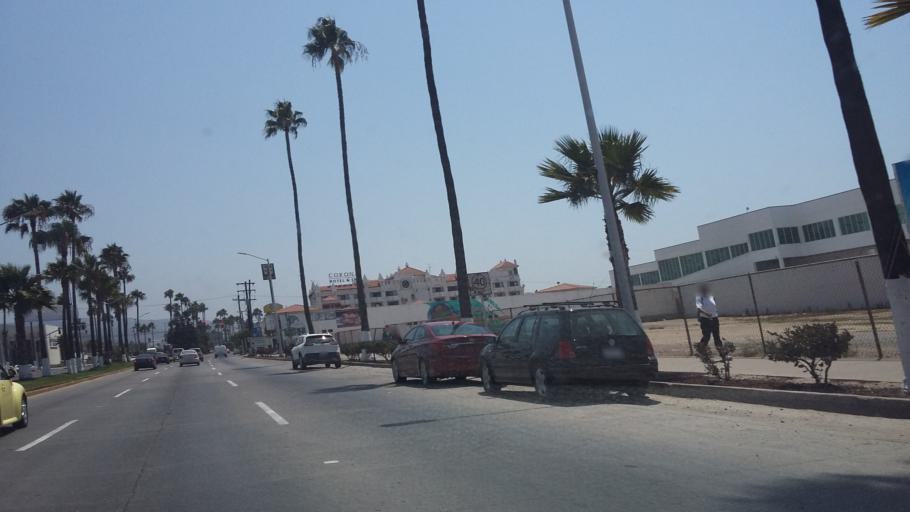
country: MX
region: Baja California
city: Ensenada
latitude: 31.8581
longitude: -116.6202
